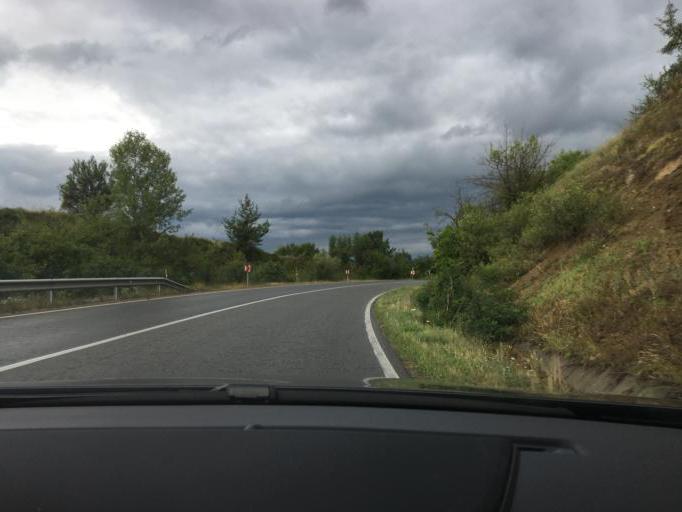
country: BG
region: Kyustendil
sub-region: Obshtina Boboshevo
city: Boboshevo
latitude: 42.2481
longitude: 22.8969
